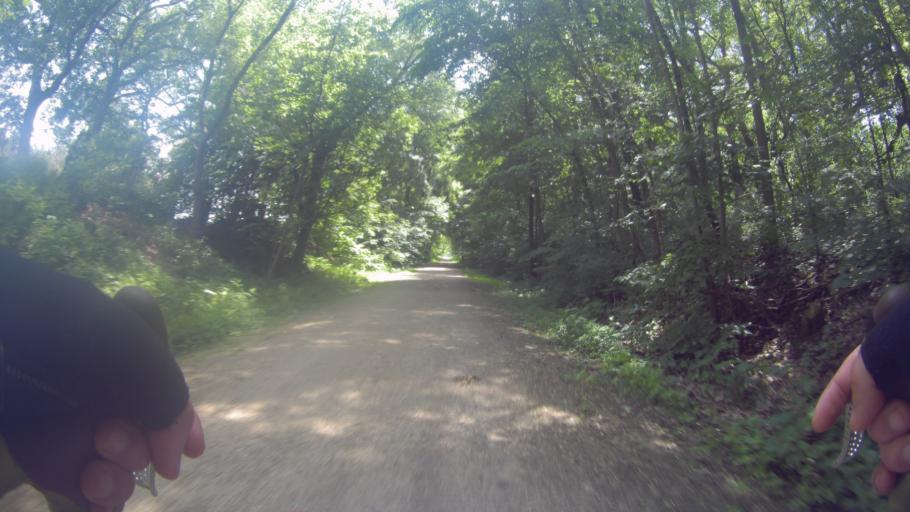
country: US
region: Wisconsin
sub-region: Jefferson County
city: Lake Mills
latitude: 43.0643
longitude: -88.9204
